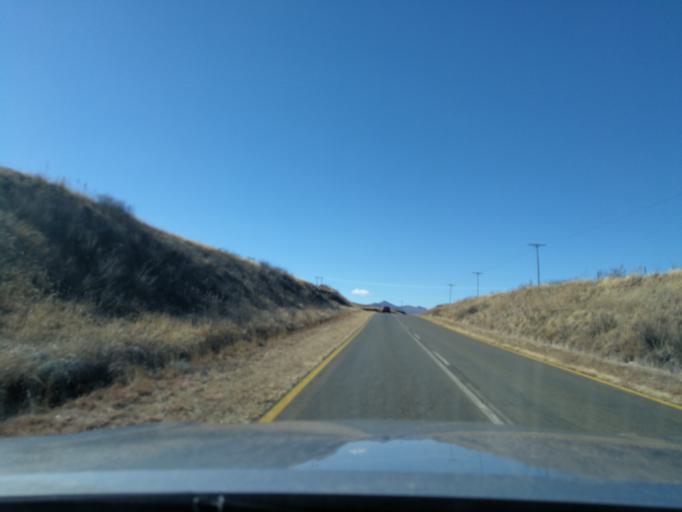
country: LS
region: Butha-Buthe
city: Butha-Buthe
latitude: -28.5280
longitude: 28.4757
